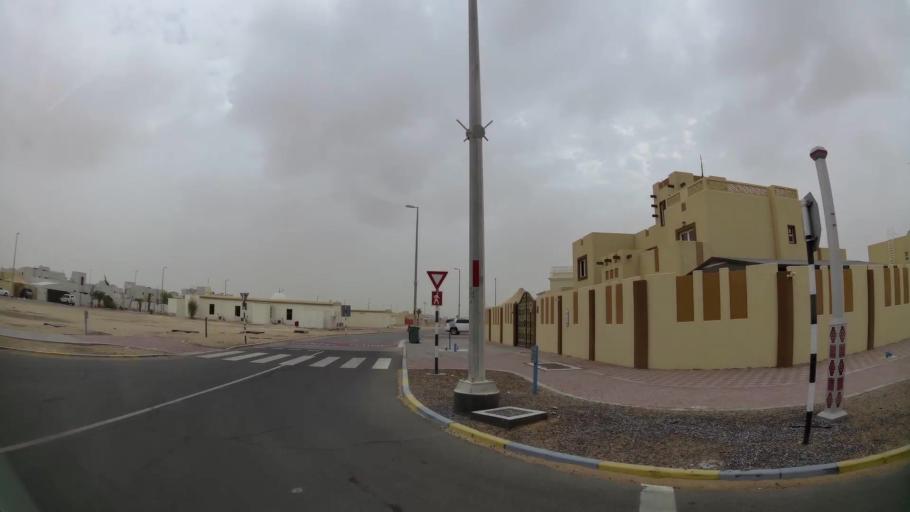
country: AE
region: Abu Dhabi
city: Abu Dhabi
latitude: 24.4451
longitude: 54.7219
